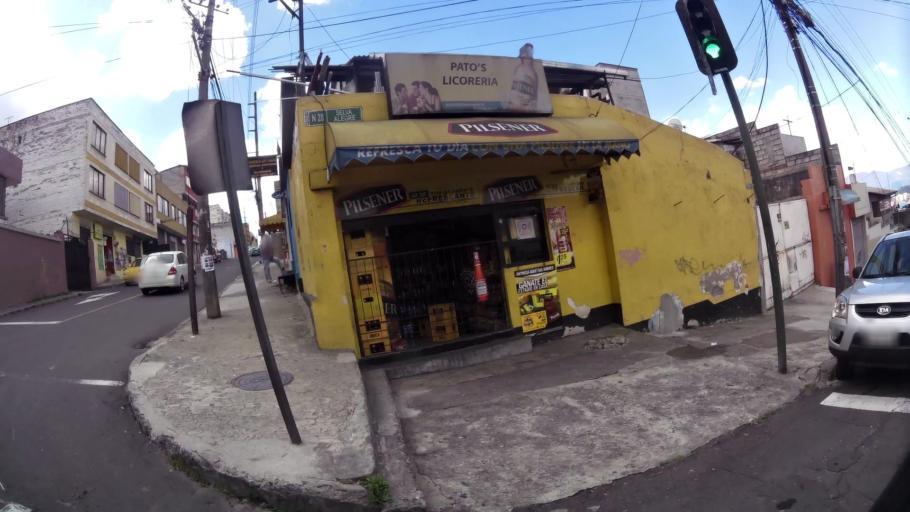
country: EC
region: Pichincha
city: Quito
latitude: -0.1868
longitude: -78.5084
